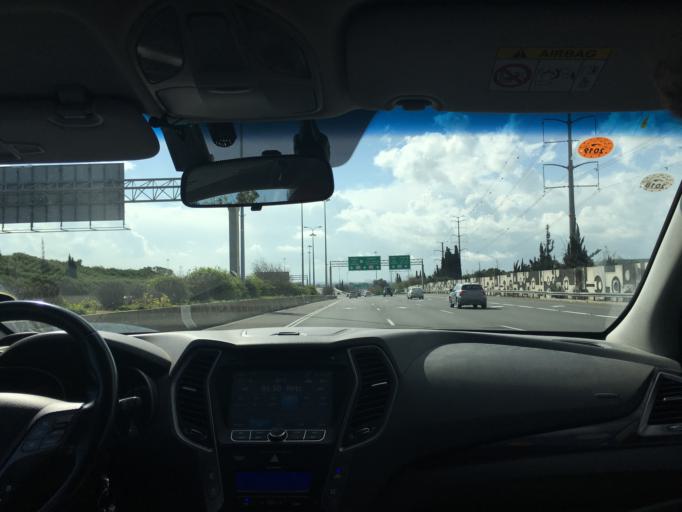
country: IL
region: Tel Aviv
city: Azor
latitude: 32.0436
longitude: 34.8296
